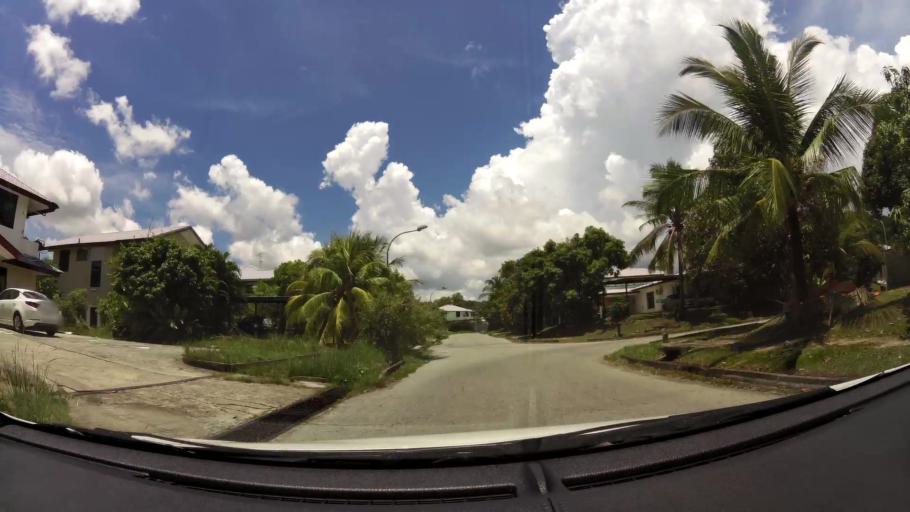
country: BN
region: Brunei and Muara
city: Bandar Seri Begawan
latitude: 4.9653
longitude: 114.9211
